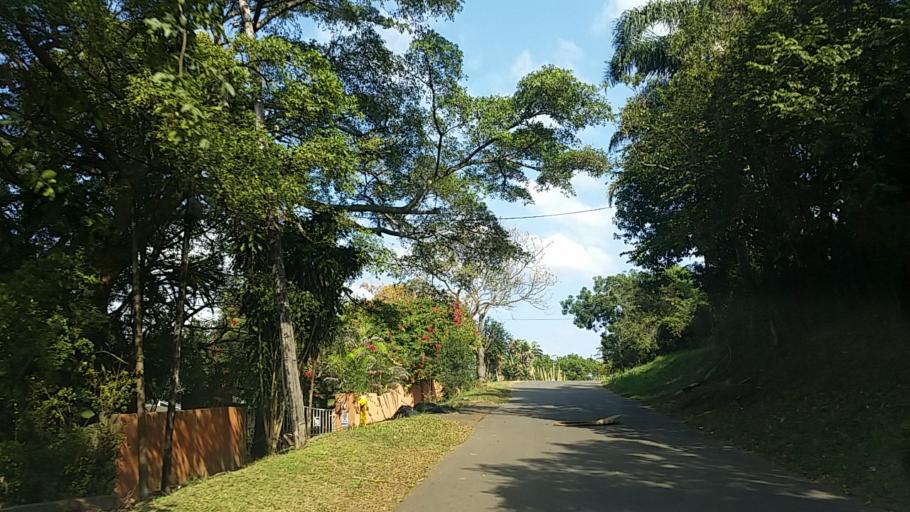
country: ZA
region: KwaZulu-Natal
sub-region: eThekwini Metropolitan Municipality
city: Berea
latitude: -29.8338
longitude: 30.9519
